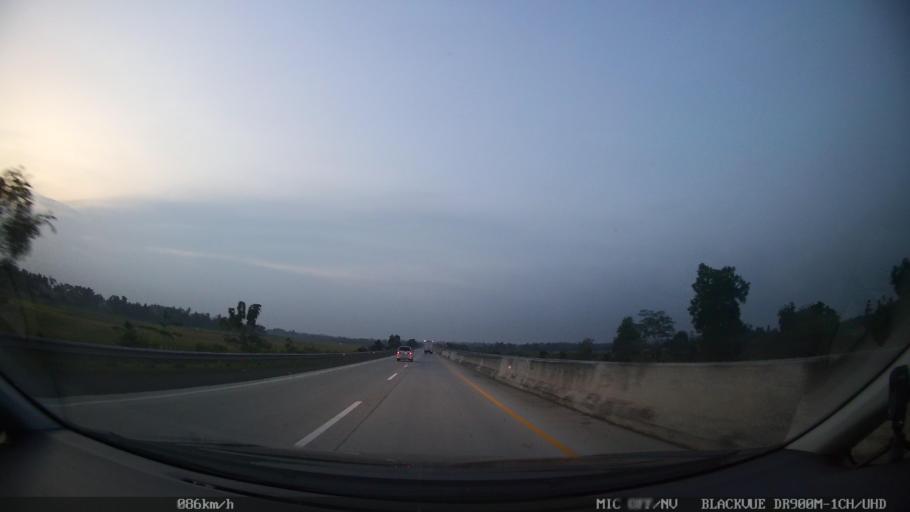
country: ID
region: Lampung
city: Sidorejo
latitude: -5.5812
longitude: 105.5427
